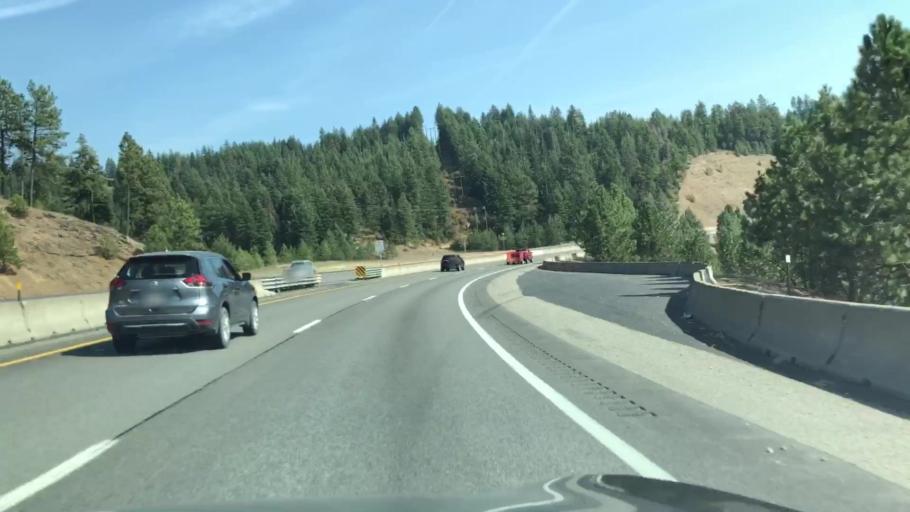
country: US
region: Idaho
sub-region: Kootenai County
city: Coeur d'Alene
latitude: 47.6627
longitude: -116.7318
